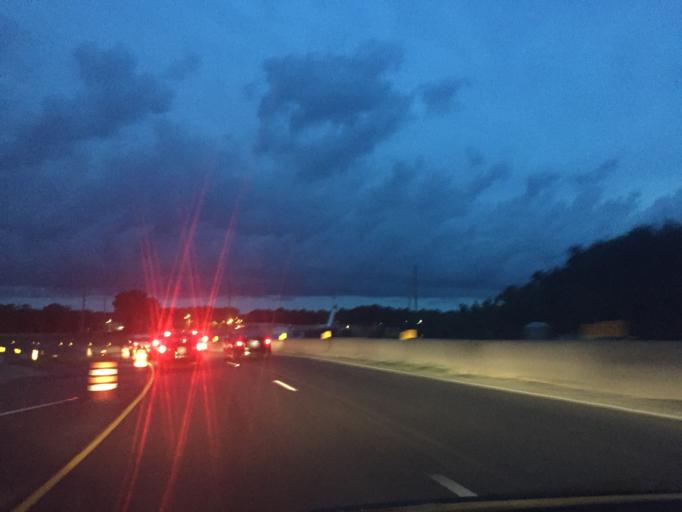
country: US
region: Georgia
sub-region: Chatham County
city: Georgetown
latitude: 31.9878
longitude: -81.2215
